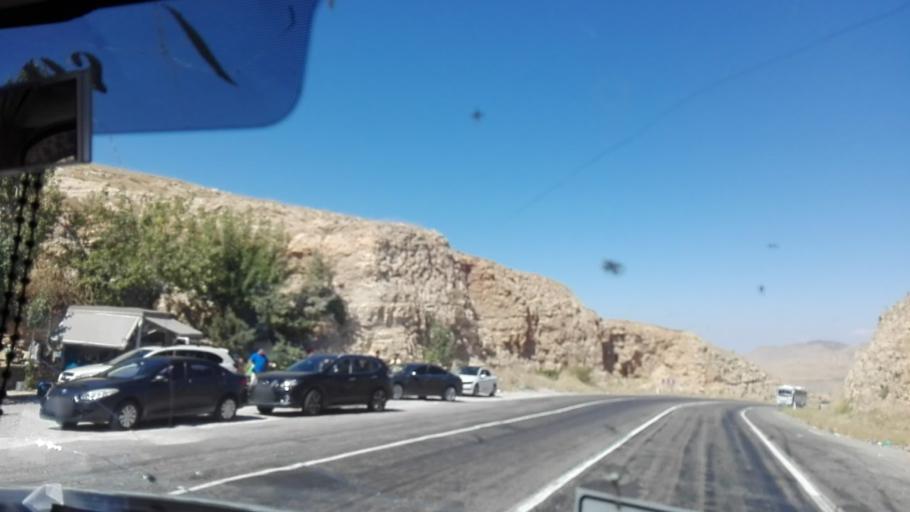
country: TR
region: Batman
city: Gerdzhyush
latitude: 37.5593
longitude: 41.3614
